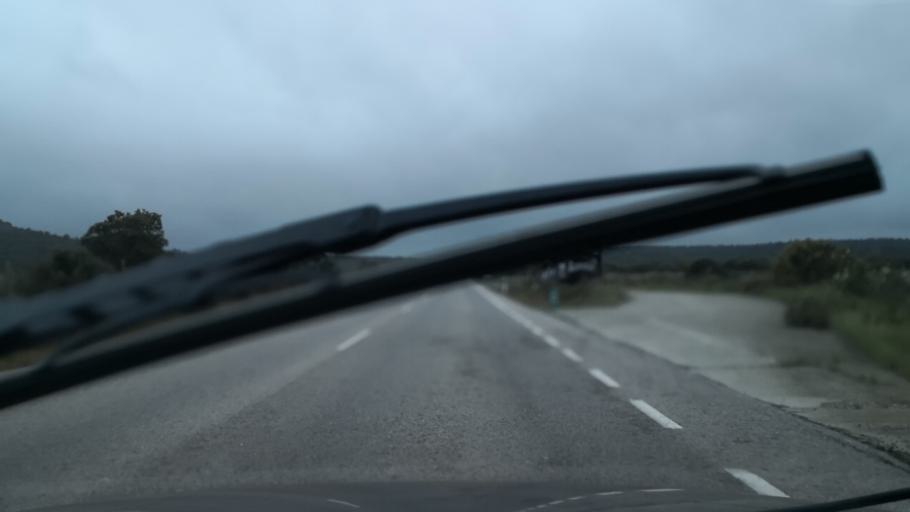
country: ES
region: Extremadura
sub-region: Provincia de Caceres
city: Malpartida de Caceres
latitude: 39.3140
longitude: -6.5079
